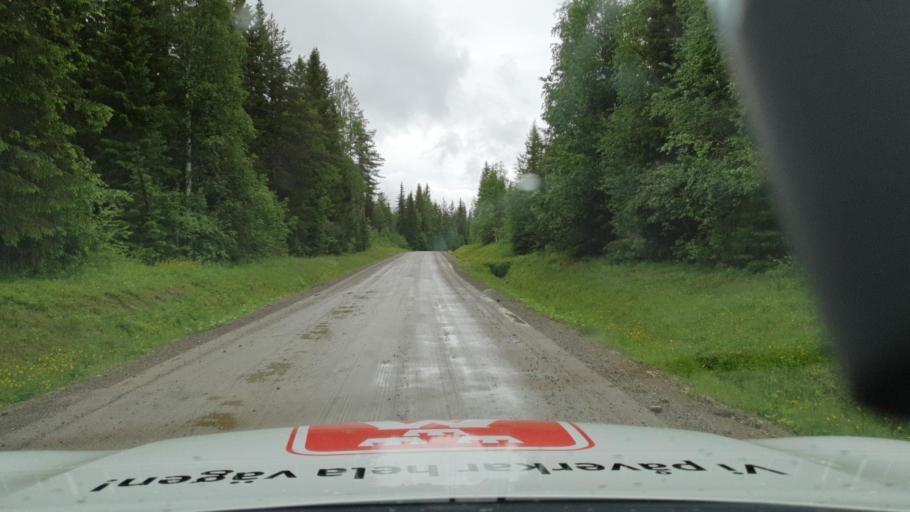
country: SE
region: Vaesterbotten
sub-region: Dorotea Kommun
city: Dorotea
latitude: 64.0544
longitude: 16.7248
